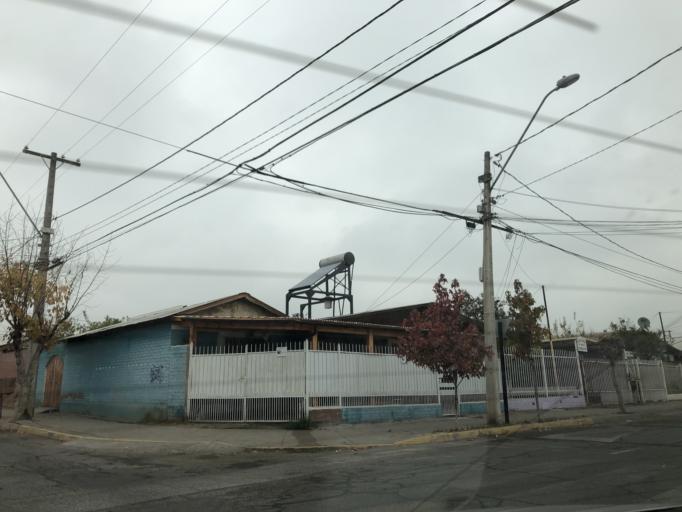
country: CL
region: Santiago Metropolitan
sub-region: Provincia de Cordillera
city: Puente Alto
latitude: -33.5906
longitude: -70.5937
